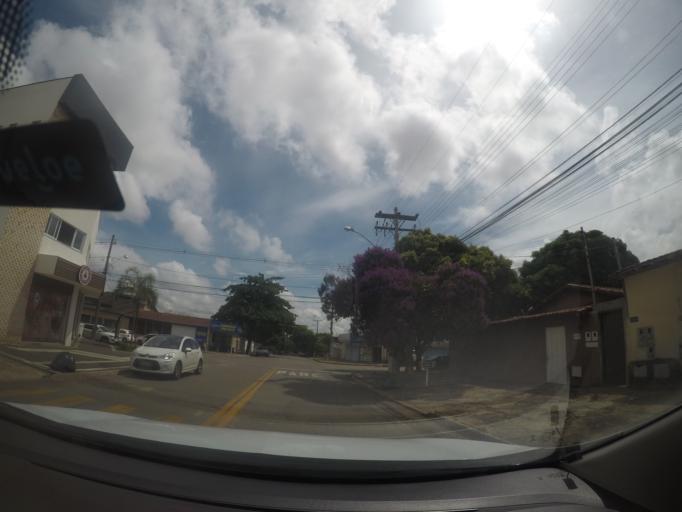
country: BR
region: Goias
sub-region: Goiania
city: Goiania
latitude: -16.7174
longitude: -49.3176
